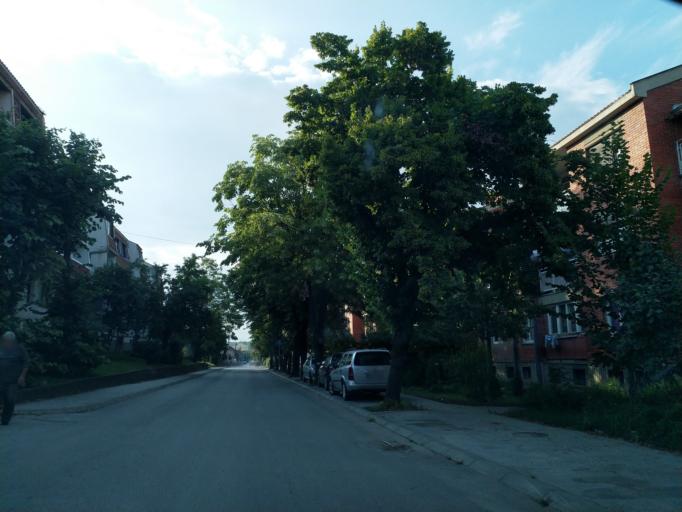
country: RS
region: Central Serbia
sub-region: Pomoravski Okrug
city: Jagodina
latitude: 43.9790
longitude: 21.2473
